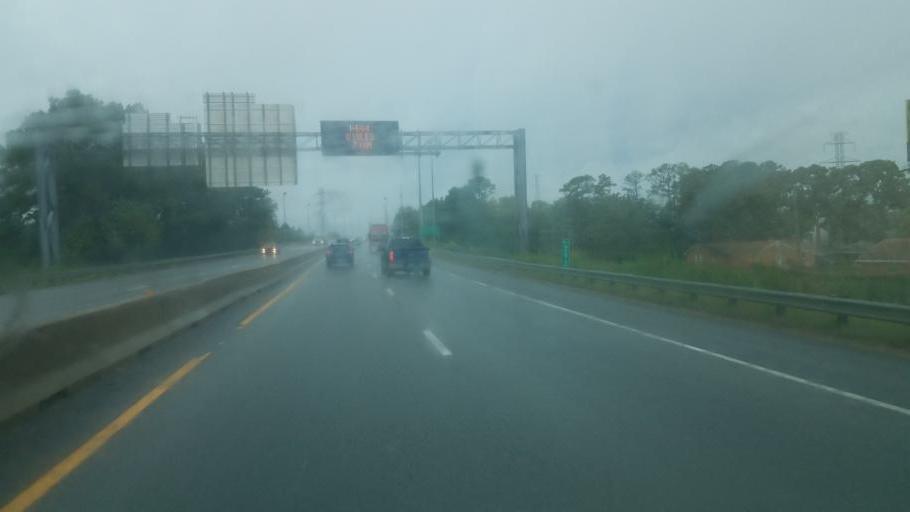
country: US
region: Virginia
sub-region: City of Chesapeake
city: Chesapeake
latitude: 36.7577
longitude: -76.2858
